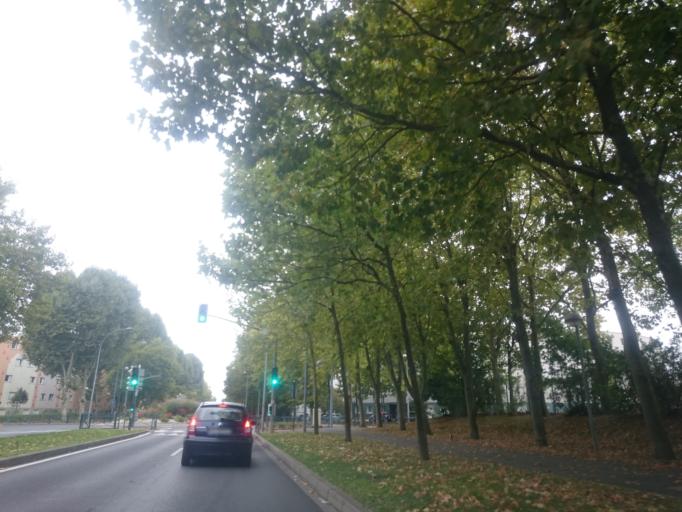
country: FR
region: Ile-de-France
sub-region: Departement de l'Essonne
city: Fleury-Merogis
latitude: 48.6482
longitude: 2.3725
